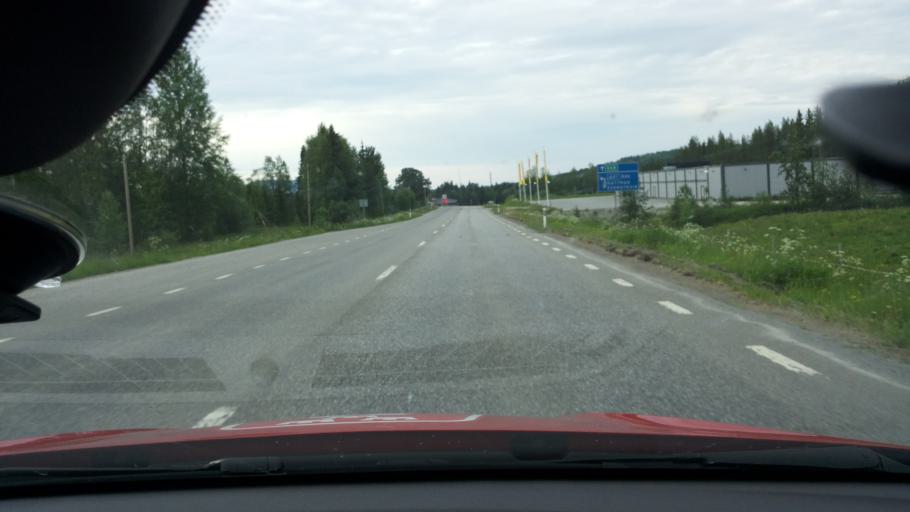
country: SE
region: Jaemtland
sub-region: Bergs Kommun
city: Hoverberg
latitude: 62.7481
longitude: 14.4257
